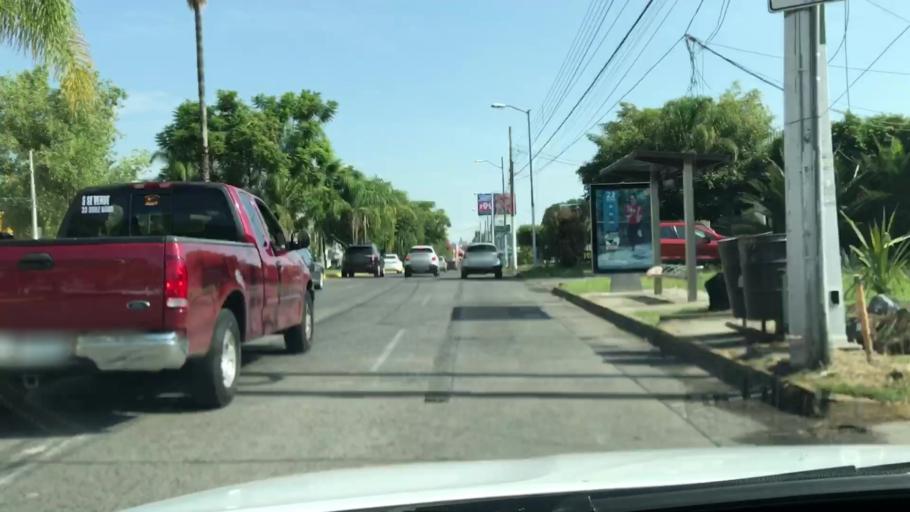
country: MX
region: Jalisco
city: Guadalajara
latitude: 20.6651
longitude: -103.4240
